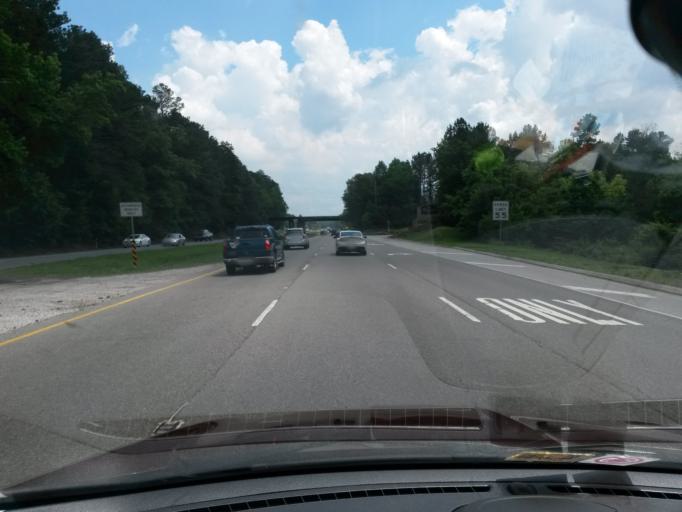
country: US
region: Virginia
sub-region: Chesterfield County
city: Enon
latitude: 37.3377
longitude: -77.3301
